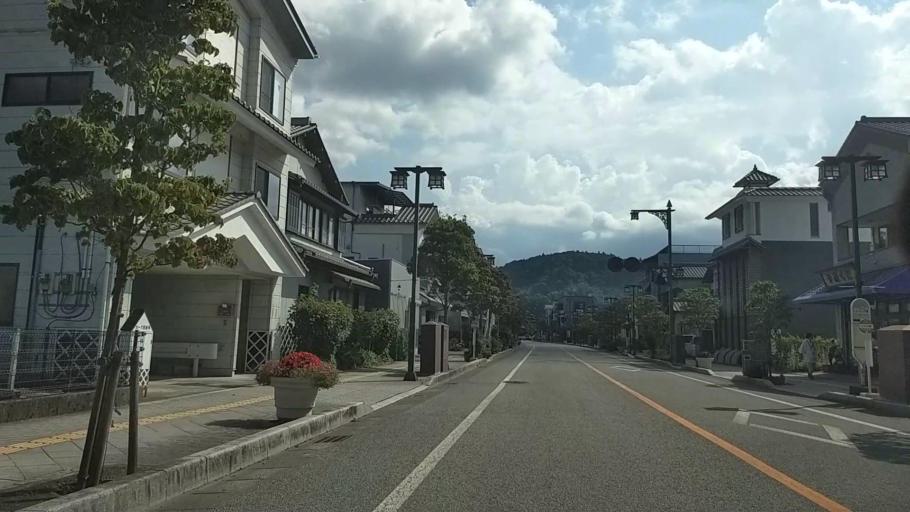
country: JP
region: Shizuoka
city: Fujinomiya
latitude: 35.3630
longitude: 138.4528
